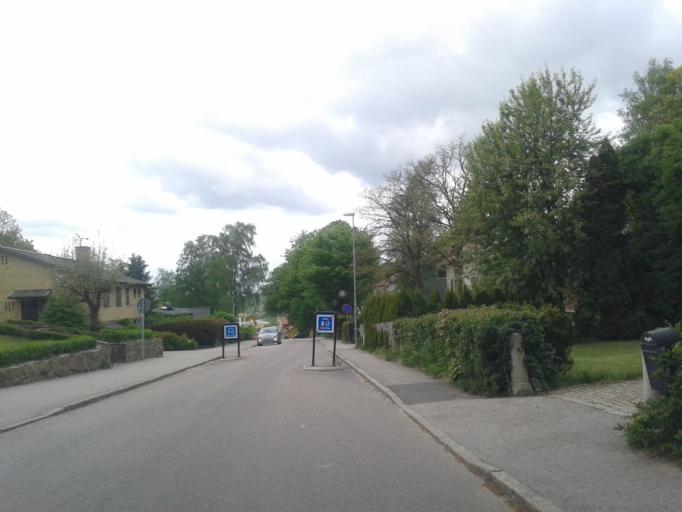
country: SE
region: Vaestra Goetaland
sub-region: Kungalvs Kommun
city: Kungalv
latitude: 57.8707
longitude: 11.9883
